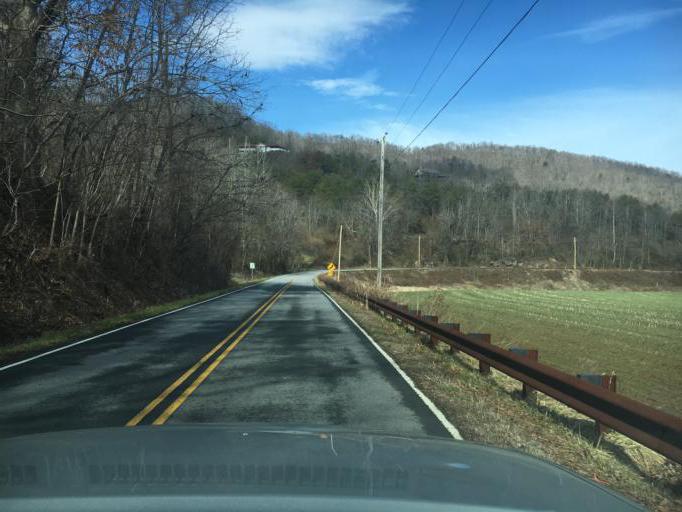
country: US
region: North Carolina
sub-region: Haywood County
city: Clyde
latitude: 35.4935
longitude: -82.8841
